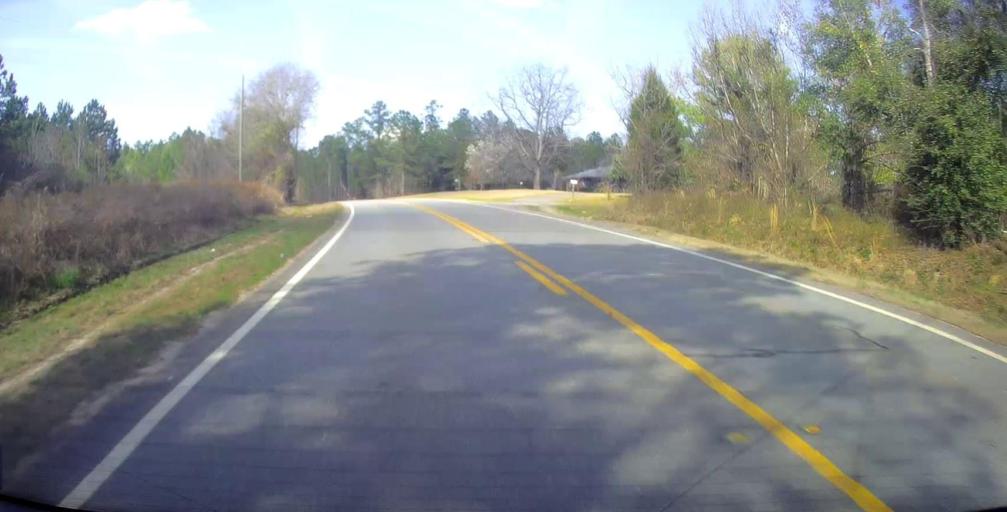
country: US
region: Georgia
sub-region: Wilkinson County
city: Gordon
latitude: 32.7844
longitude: -83.3299
